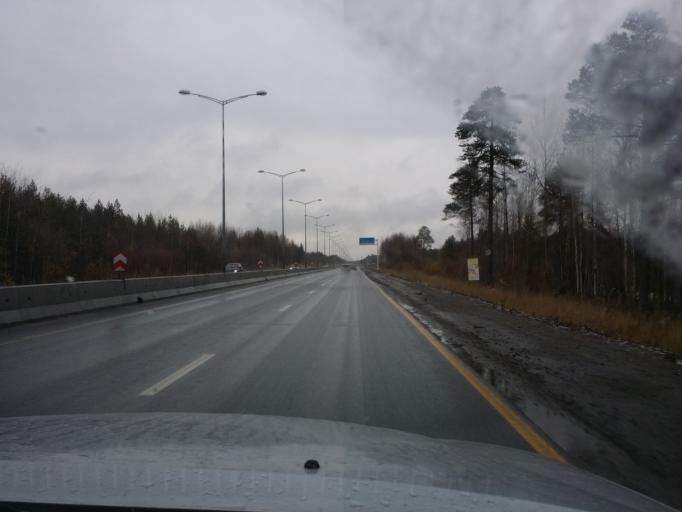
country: RU
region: Khanty-Mansiyskiy Avtonomnyy Okrug
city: Nizhnevartovsk
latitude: 61.0027
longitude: 76.4163
